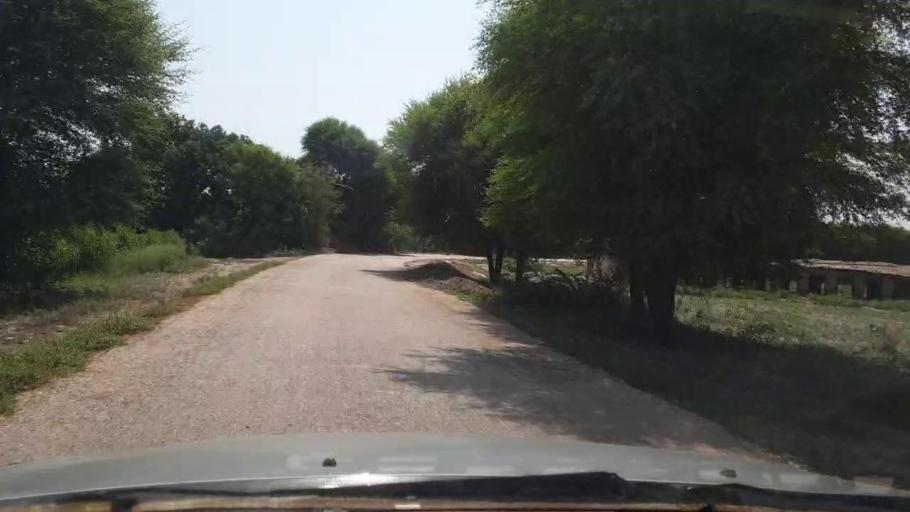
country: PK
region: Sindh
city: Chambar
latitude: 25.2305
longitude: 68.7773
